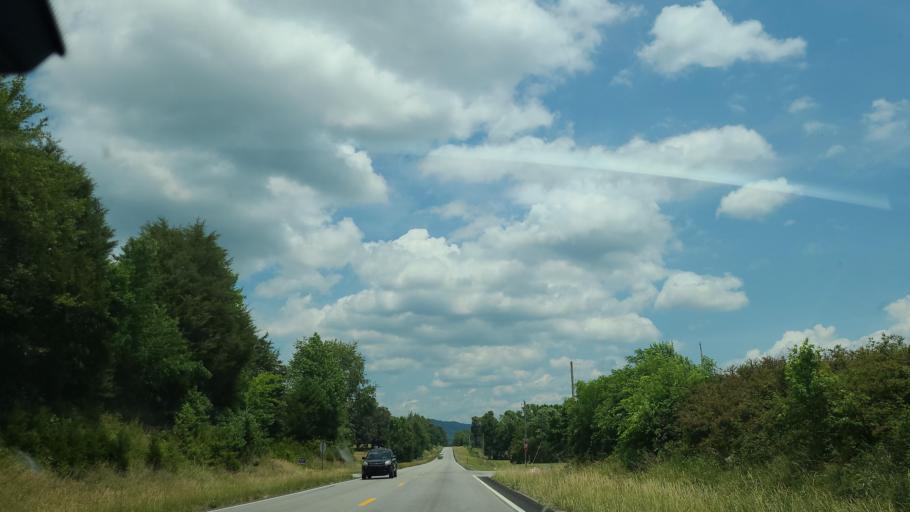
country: US
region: Tennessee
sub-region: Bledsoe County
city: Pikeville
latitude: 35.7147
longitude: -85.0952
